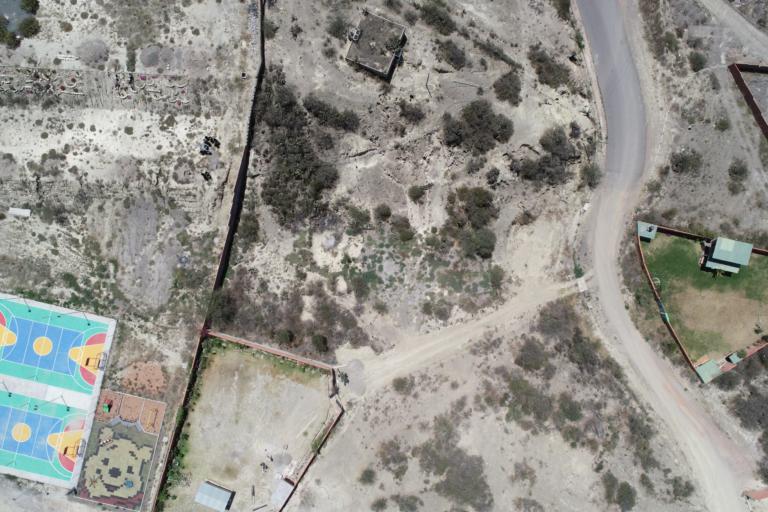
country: BO
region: La Paz
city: La Paz
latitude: -16.6210
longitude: -68.0576
